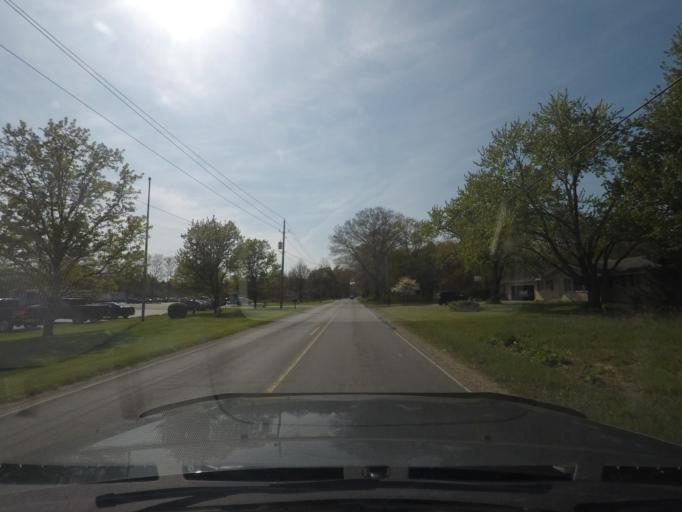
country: US
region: Indiana
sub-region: Elkhart County
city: Elkhart
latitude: 41.7050
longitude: -86.0112
